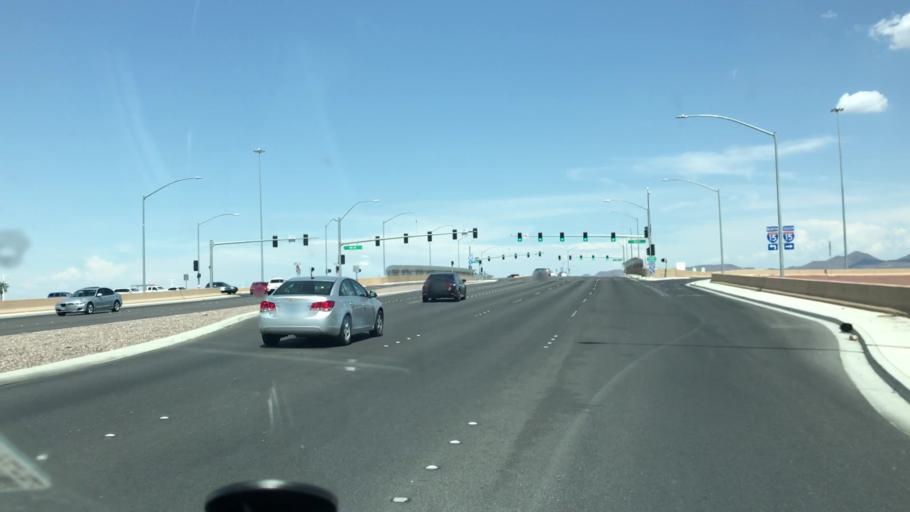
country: US
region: Nevada
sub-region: Clark County
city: Enterprise
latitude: 35.9989
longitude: -115.1828
